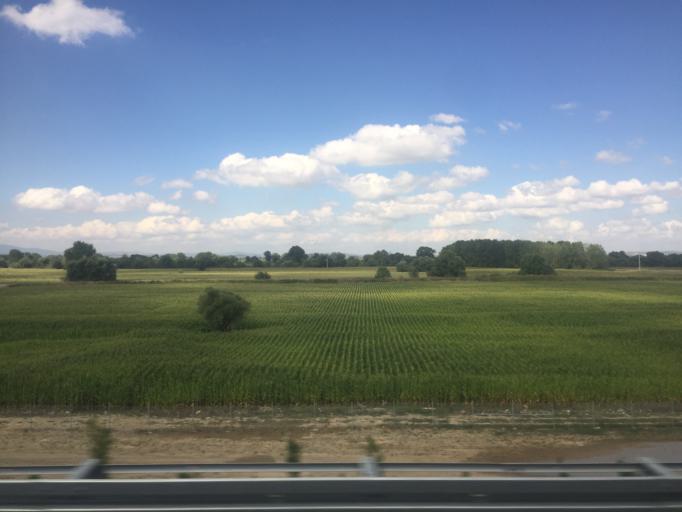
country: TR
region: Bursa
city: Tatkavakli
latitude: 40.1096
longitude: 28.2771
